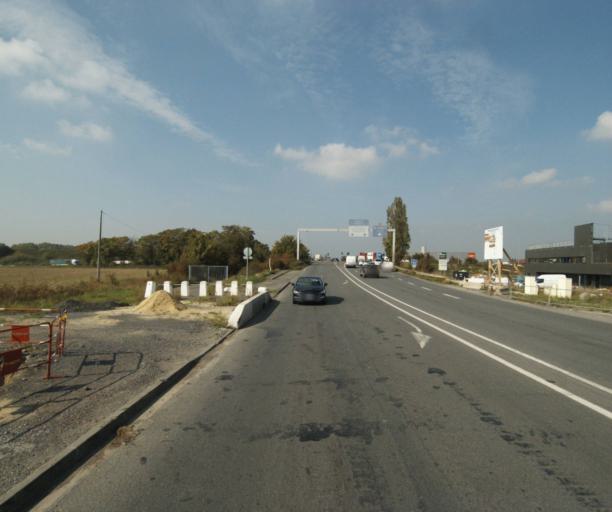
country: FR
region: Nord-Pas-de-Calais
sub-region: Departement du Nord
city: Attiches
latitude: 50.5442
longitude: 3.0585
